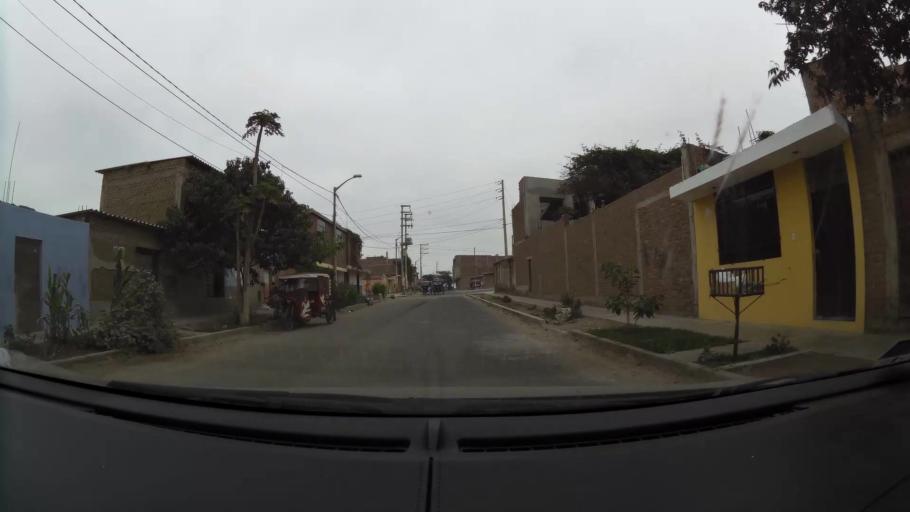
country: PE
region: La Libertad
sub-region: Provincia de Trujillo
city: La Esperanza
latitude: -8.0816
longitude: -79.0541
